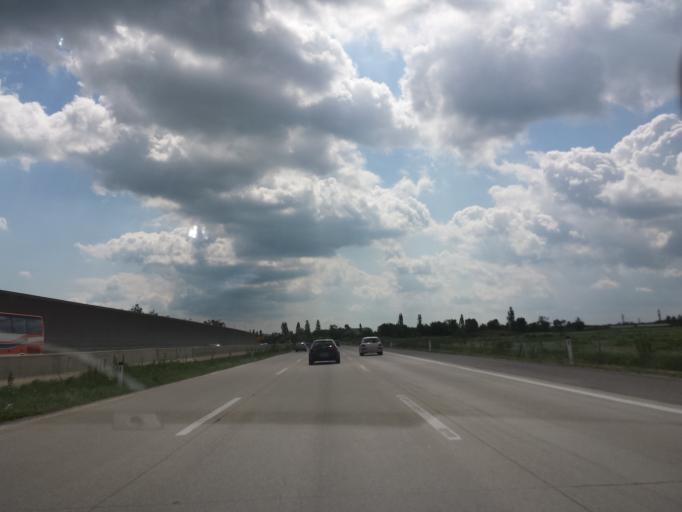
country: AT
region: Lower Austria
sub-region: Politischer Bezirk Wien-Umgebung
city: Rauchenwarth
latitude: 48.1382
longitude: 16.5255
